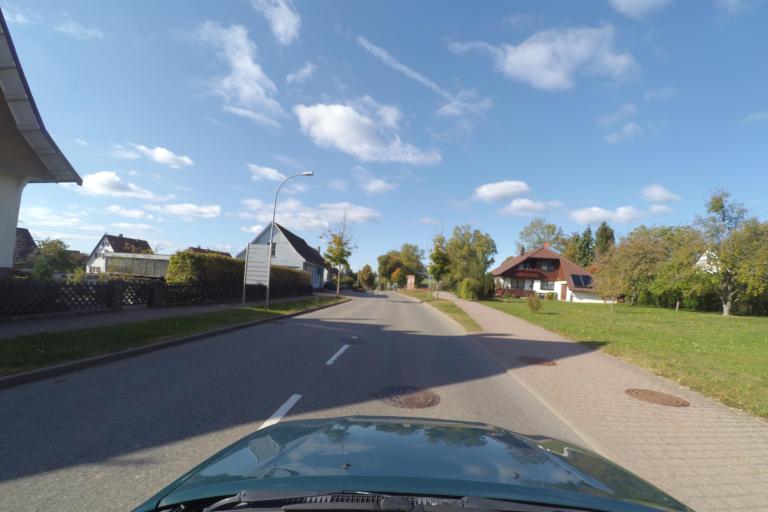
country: DE
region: Baden-Wuerttemberg
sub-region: Karlsruhe Region
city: Neubulach
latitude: 48.6633
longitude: 8.6912
